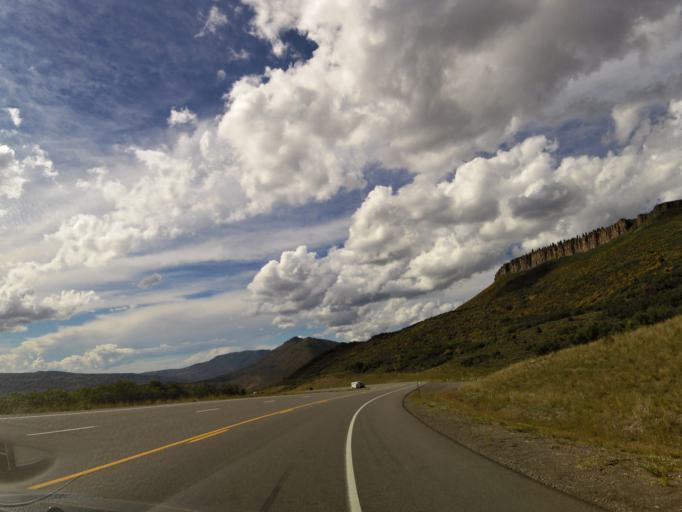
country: US
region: Colorado
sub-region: Hinsdale County
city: Lake City
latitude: 38.3942
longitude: -107.4466
